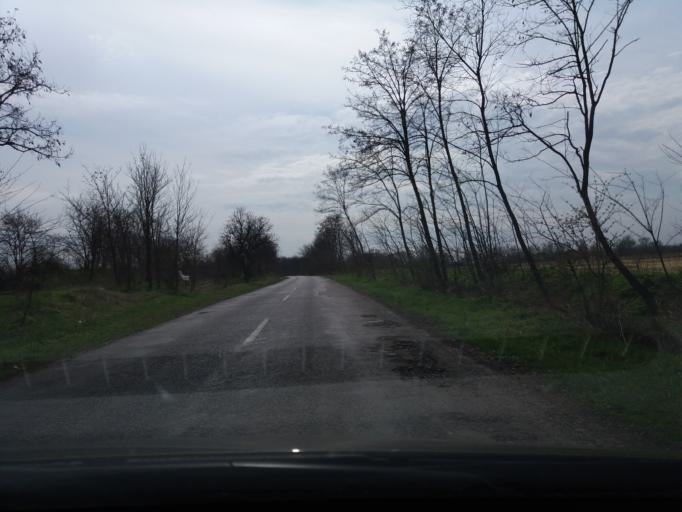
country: HU
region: Szabolcs-Szatmar-Bereg
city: Petnehaza
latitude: 48.0737
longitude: 22.0886
